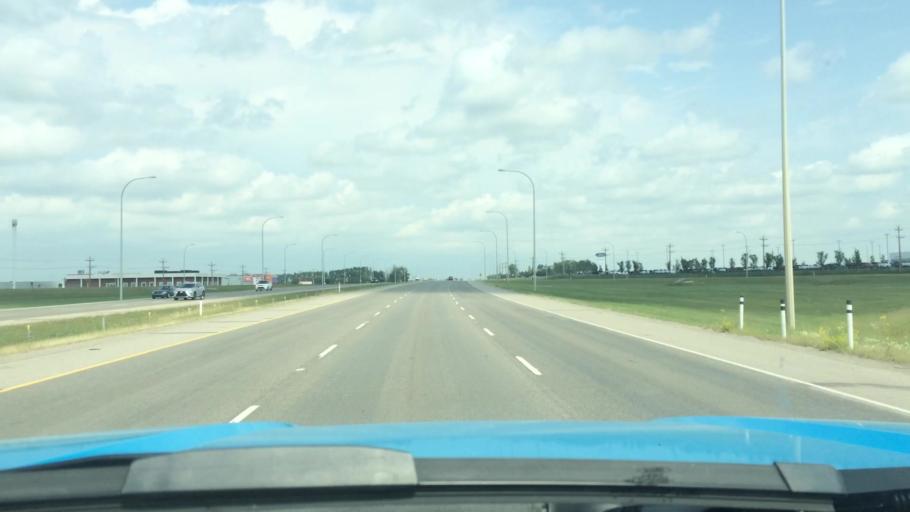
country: CA
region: Alberta
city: Airdrie
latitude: 51.3009
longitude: -114.0017
